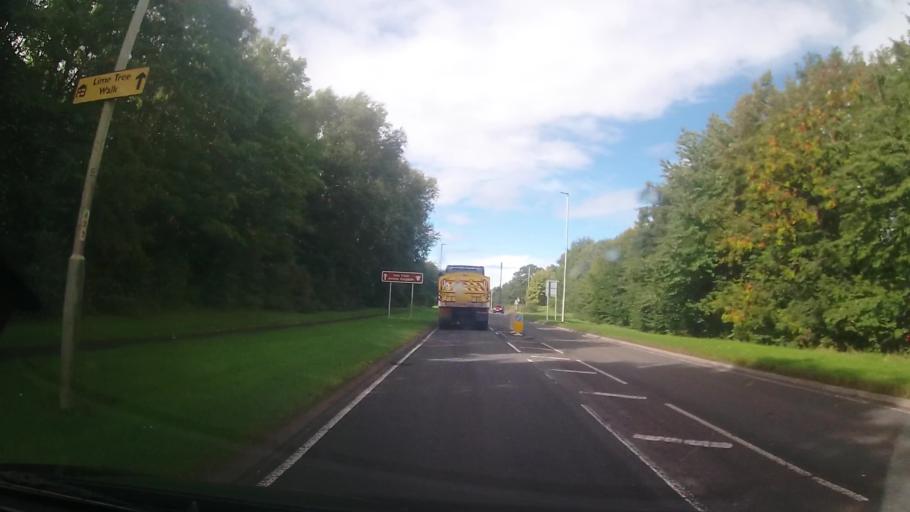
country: GB
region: England
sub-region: Telford and Wrekin
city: Wellington
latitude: 52.7085
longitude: -2.5109
